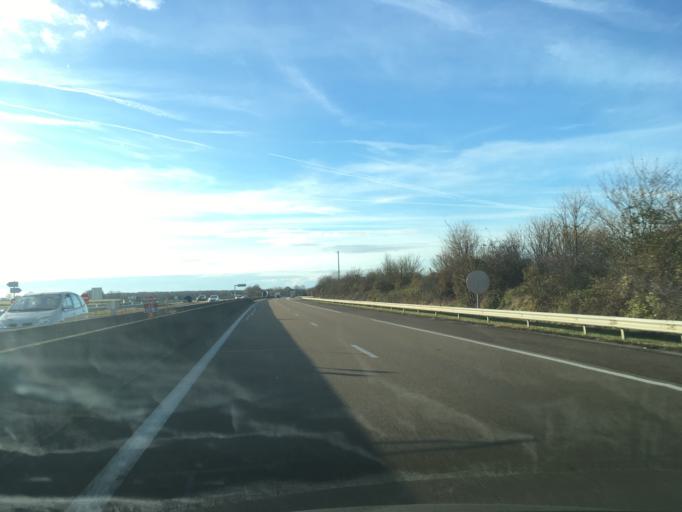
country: FR
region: Bourgogne
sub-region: Departement de l'Yonne
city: Avallon
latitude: 47.5038
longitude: 4.0348
